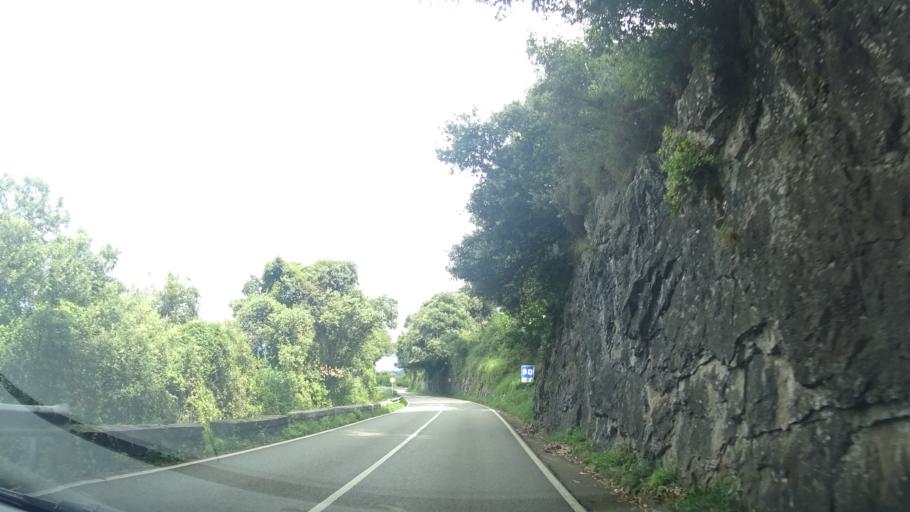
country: ES
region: Asturias
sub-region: Province of Asturias
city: Ribadesella
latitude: 43.4639
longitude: -5.1050
